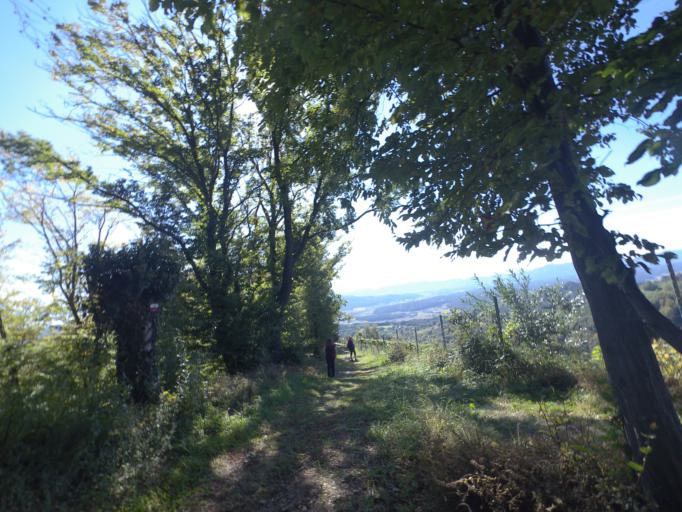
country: AT
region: Styria
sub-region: Politischer Bezirk Leibnitz
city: Kitzeck im Sausal
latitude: 46.7814
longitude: 15.4331
